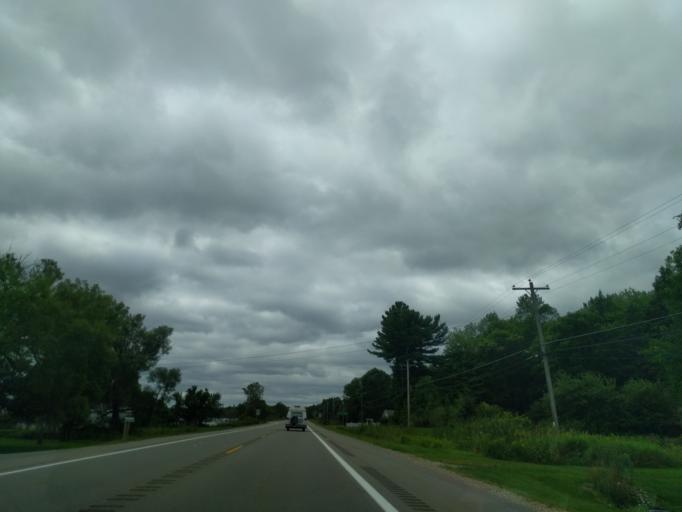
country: US
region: Michigan
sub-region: Menominee County
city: Menominee
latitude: 45.1887
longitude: -87.5557
